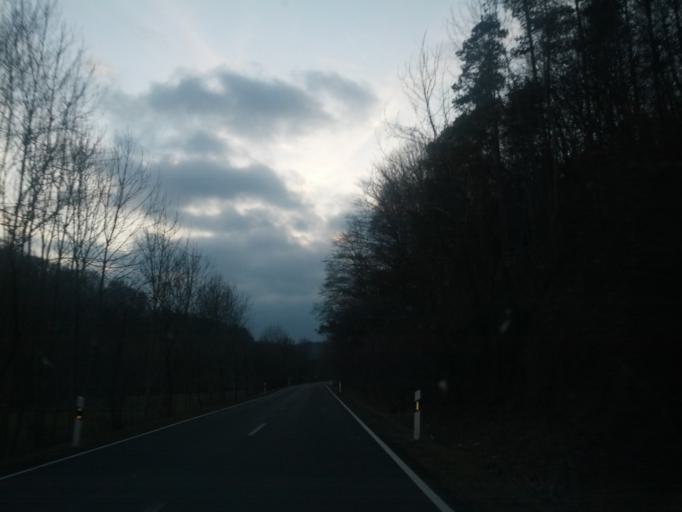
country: DE
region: Thuringia
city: Treffurt
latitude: 51.1472
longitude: 10.2316
